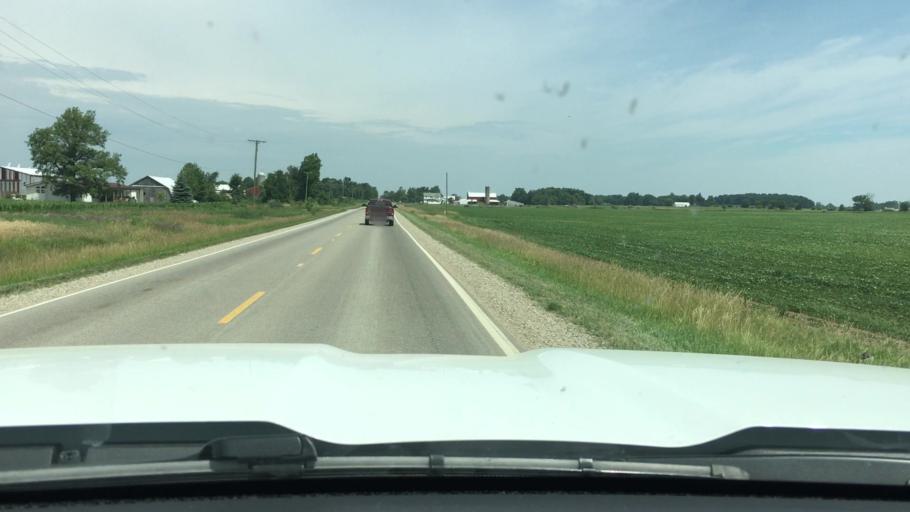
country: US
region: Michigan
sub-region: Sanilac County
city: Brown City
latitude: 43.2876
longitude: -82.9829
